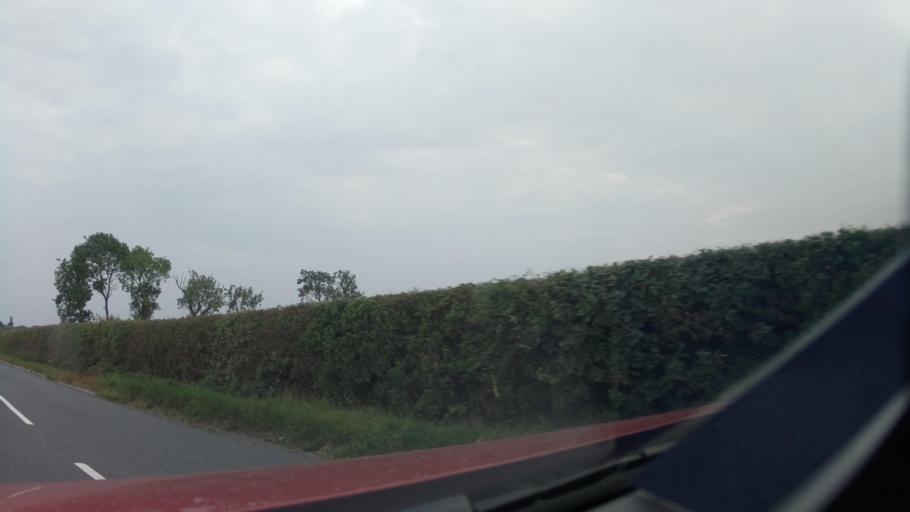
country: GB
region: England
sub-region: Lincolnshire
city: Skellingthorpe
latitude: 53.1386
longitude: -0.6456
